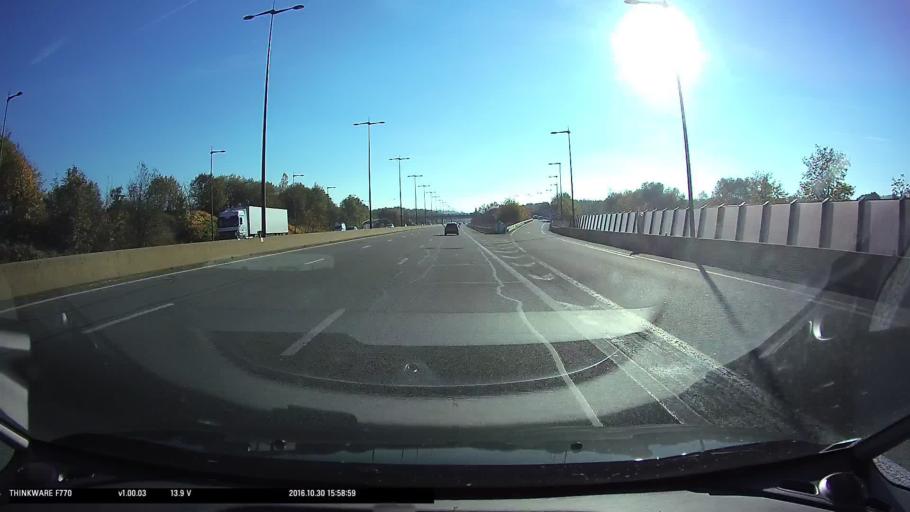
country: FR
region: Franche-Comte
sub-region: Departement du Doubs
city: Nommay
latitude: 47.5287
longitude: 6.8581
